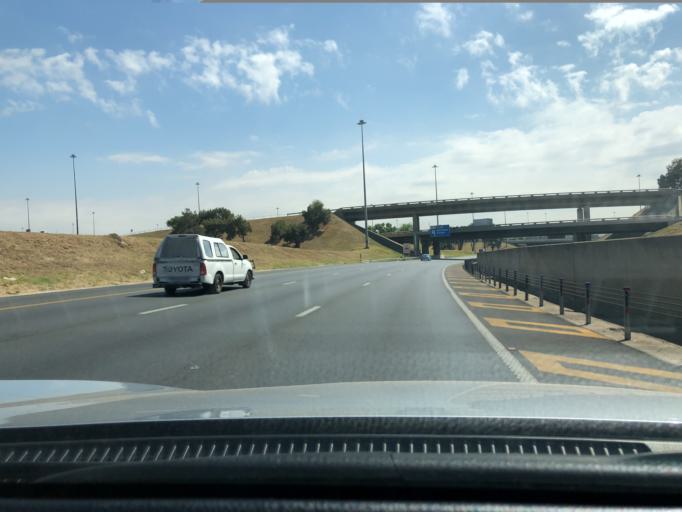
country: ZA
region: Gauteng
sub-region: City of Johannesburg Metropolitan Municipality
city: Midrand
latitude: -26.0504
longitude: 28.0940
